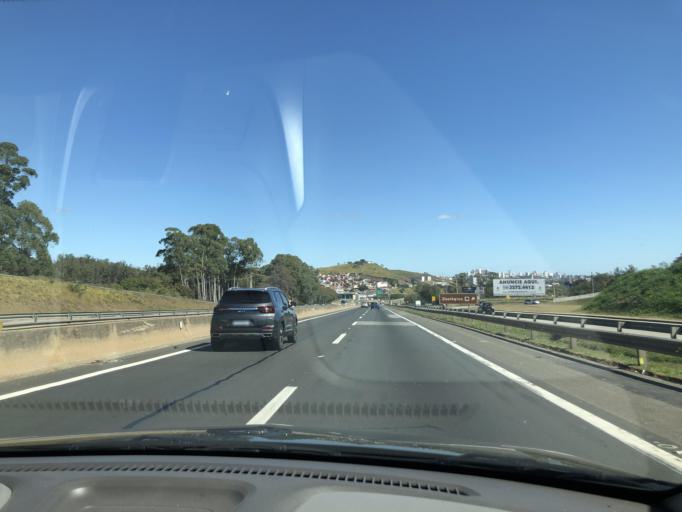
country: BR
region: Sao Paulo
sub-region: Sorocaba
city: Sorocaba
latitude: -23.5089
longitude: -47.4185
